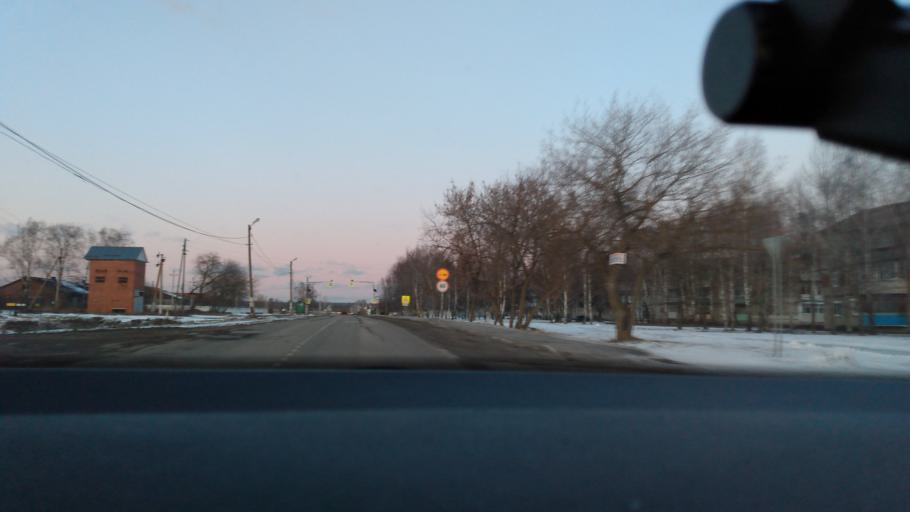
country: RU
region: Moskovskaya
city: Krasnaya Poyma
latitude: 55.1191
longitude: 39.0724
